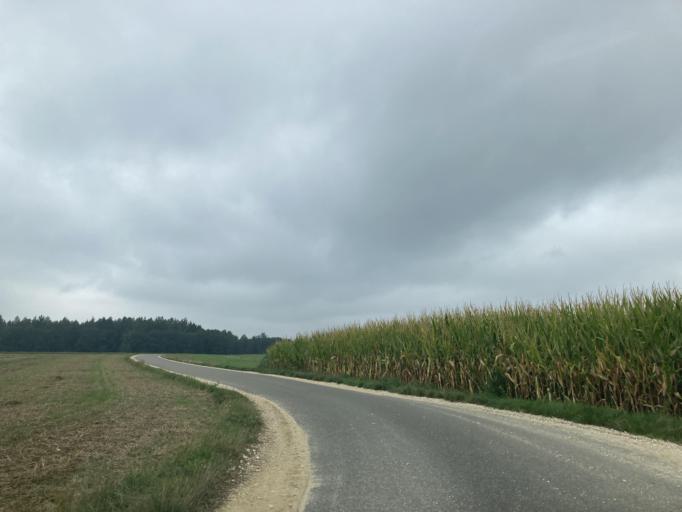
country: DE
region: Bavaria
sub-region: Swabia
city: Medlingen
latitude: 48.5792
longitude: 10.3097
